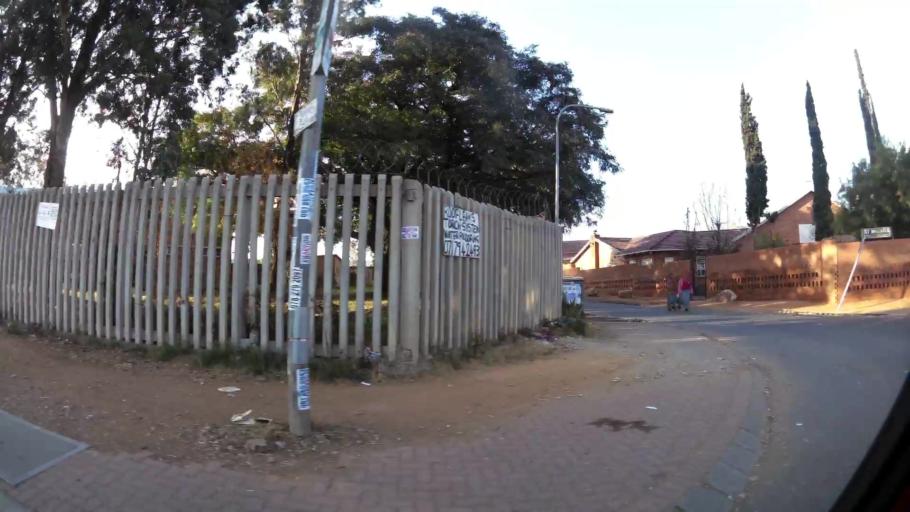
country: ZA
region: Gauteng
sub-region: City of Johannesburg Metropolitan Municipality
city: Roodepoort
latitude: -26.2166
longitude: 27.8961
